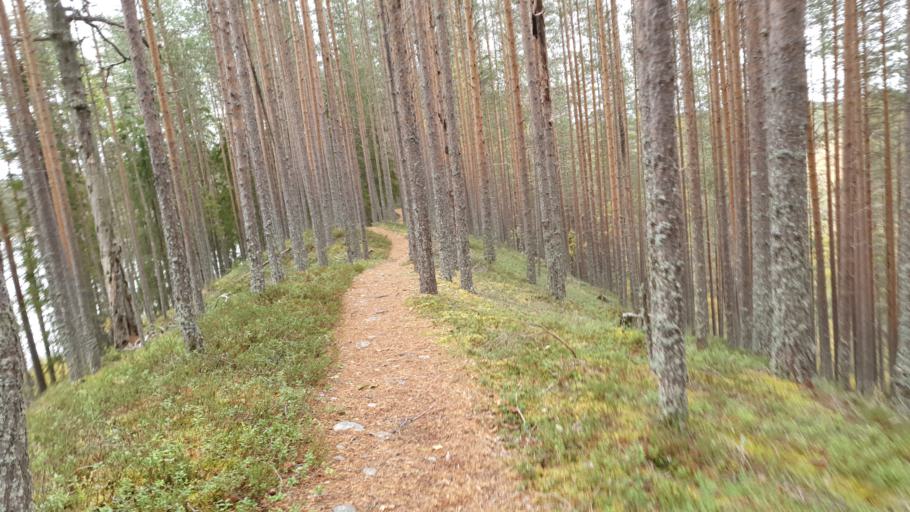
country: FI
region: Kainuu
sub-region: Kehys-Kainuu
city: Kuhmo
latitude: 64.2932
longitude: 29.3491
